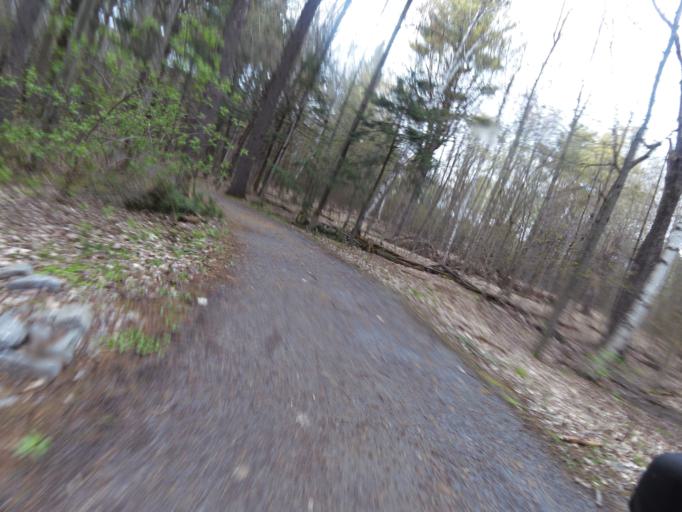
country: CA
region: Ontario
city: Bells Corners
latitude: 45.3203
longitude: -75.7919
